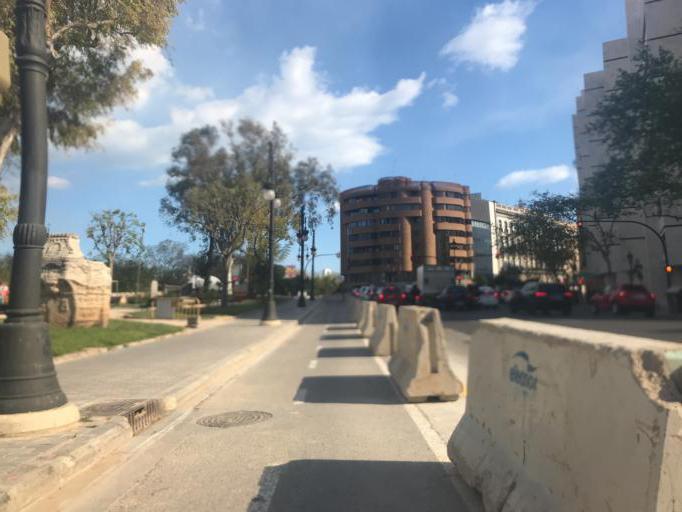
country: ES
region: Valencia
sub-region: Provincia de Valencia
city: Valencia
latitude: 39.4763
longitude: -0.3703
